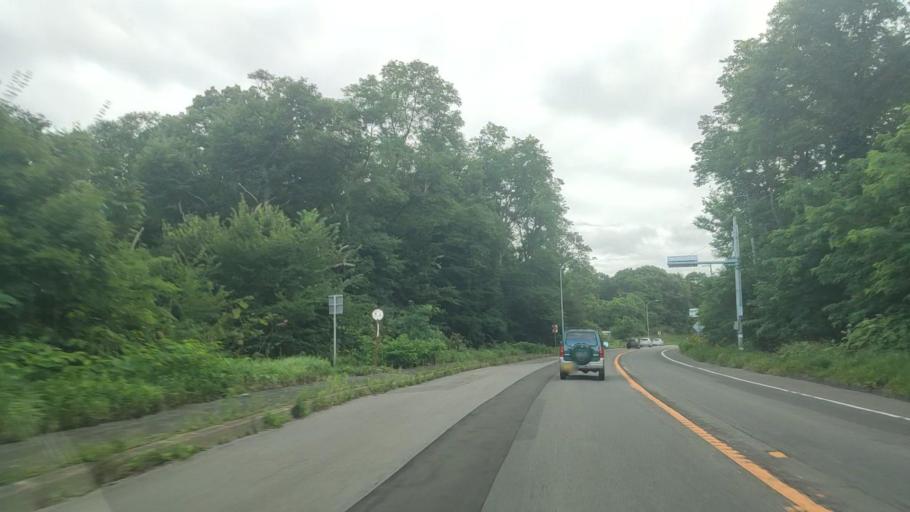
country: JP
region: Hokkaido
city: Nanae
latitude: 42.0659
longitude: 140.6030
